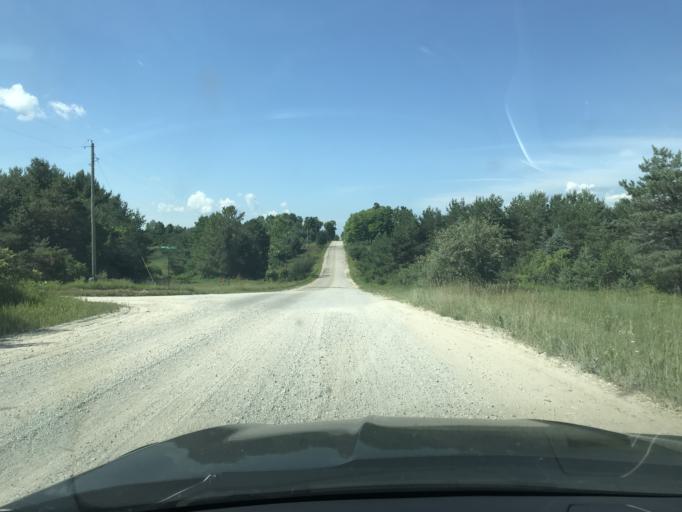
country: US
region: Michigan
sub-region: Cheboygan County
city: Cheboygan
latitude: 45.6176
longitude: -84.6714
